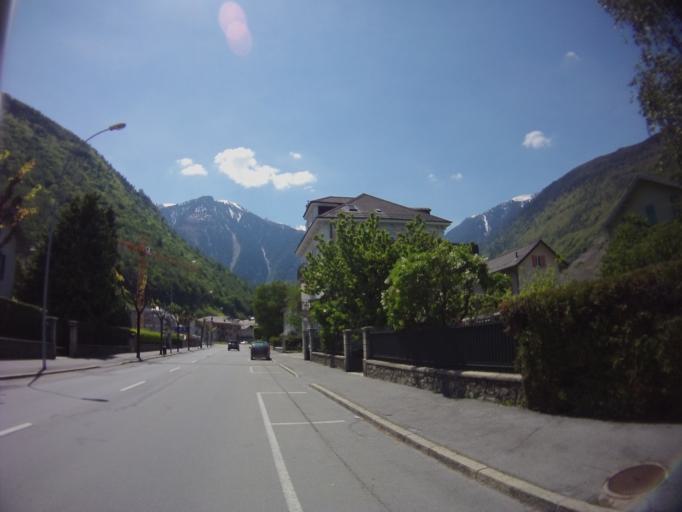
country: CH
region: Valais
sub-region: Martigny District
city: Martigny-Ville
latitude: 46.0937
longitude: 7.0664
